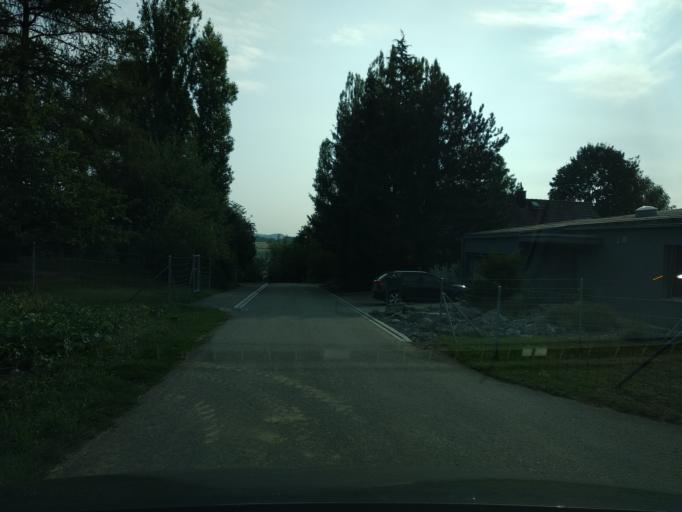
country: DE
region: Baden-Wuerttemberg
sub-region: Freiburg Region
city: Busingen
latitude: 47.6586
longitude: 8.6906
